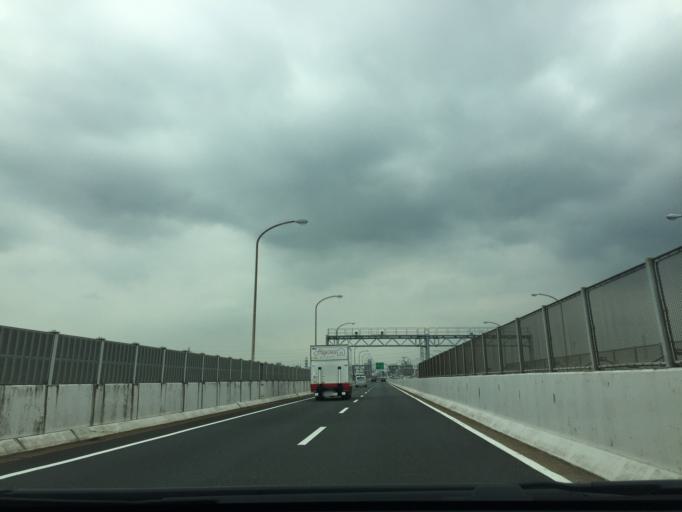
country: JP
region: Aichi
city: Obu
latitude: 35.0885
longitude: 136.9323
